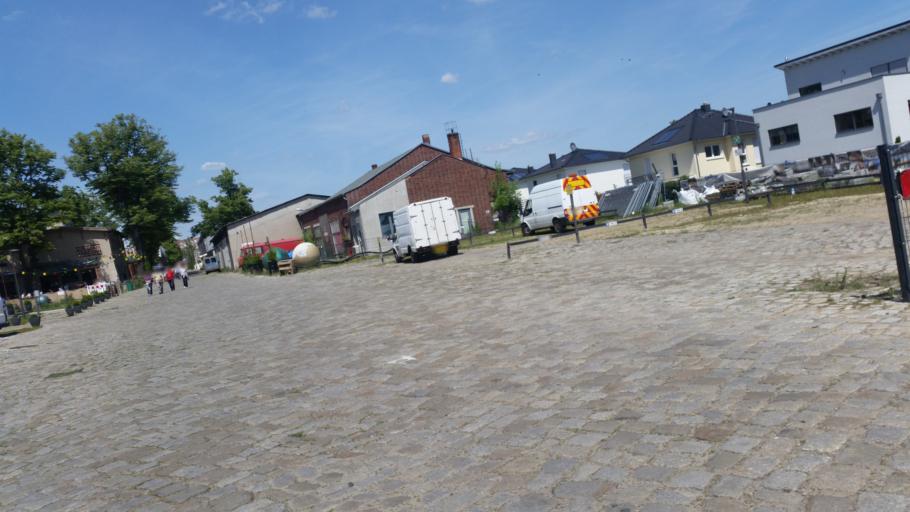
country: DE
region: Berlin
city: Friedrichsfelde
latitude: 52.5188
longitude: 13.5263
